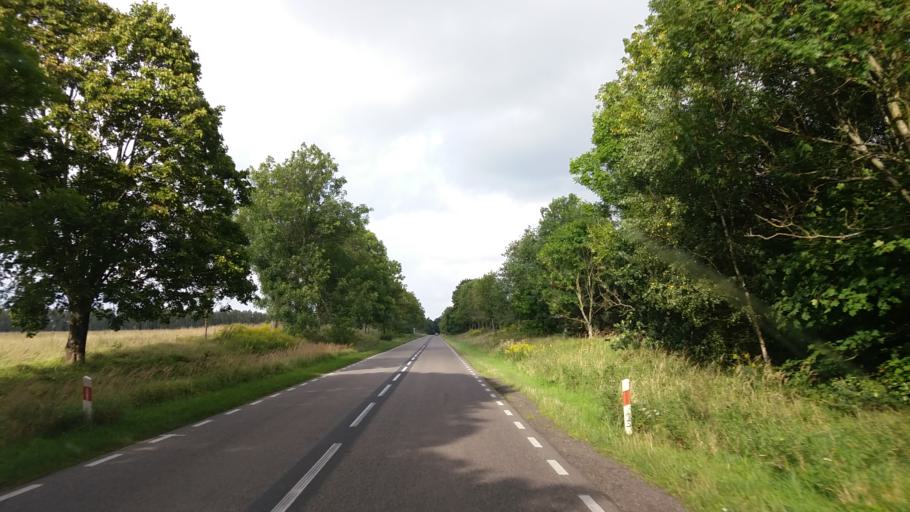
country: PL
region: West Pomeranian Voivodeship
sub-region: Powiat mysliborski
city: Barlinek
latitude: 53.0068
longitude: 15.2532
